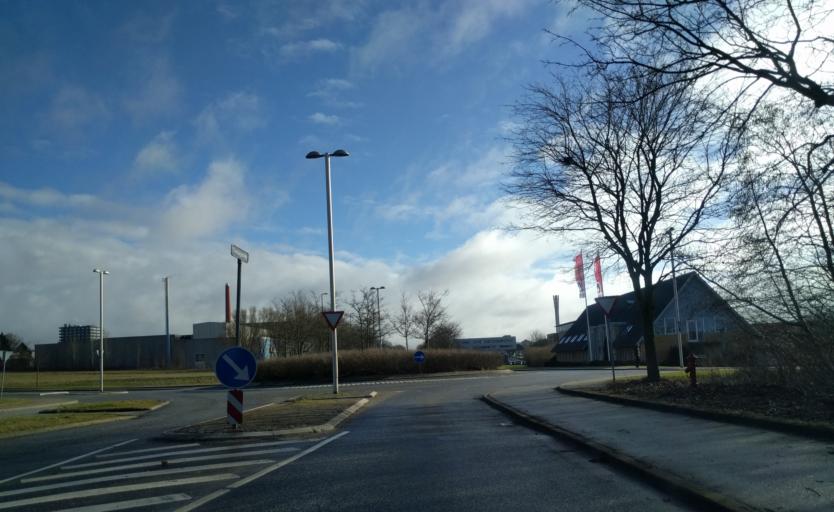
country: DK
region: North Denmark
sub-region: Alborg Kommune
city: Aalborg
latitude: 57.0240
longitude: 9.8877
